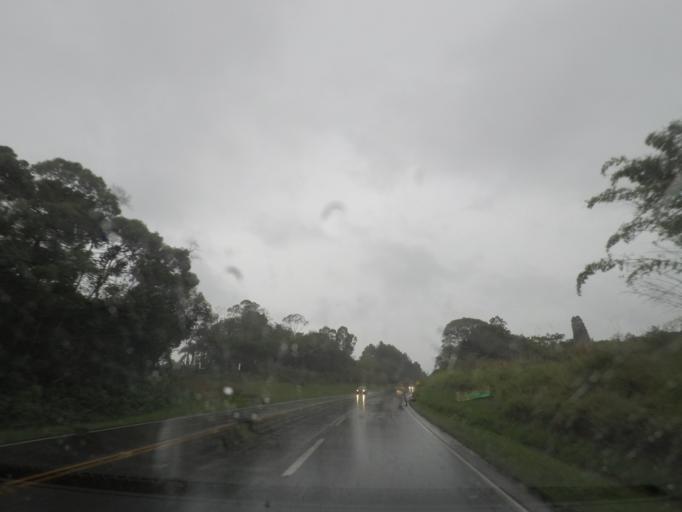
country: BR
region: Parana
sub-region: Almirante Tamandare
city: Almirante Tamandare
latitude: -25.3537
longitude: -49.3051
